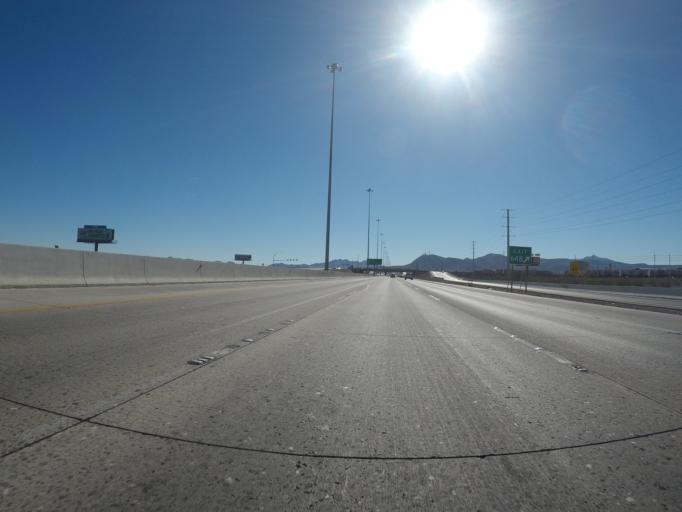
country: US
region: Nevada
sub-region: Clark County
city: Whitney
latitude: 36.0756
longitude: -115.0392
